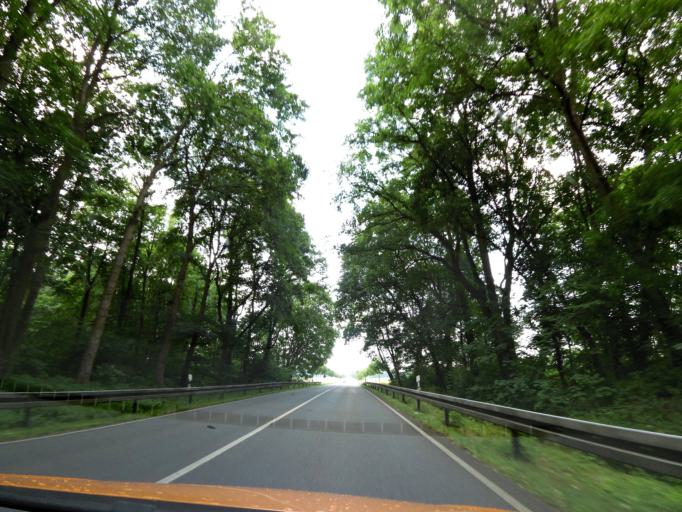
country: DE
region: Brandenburg
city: Dreetz
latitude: 52.8213
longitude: 12.5361
